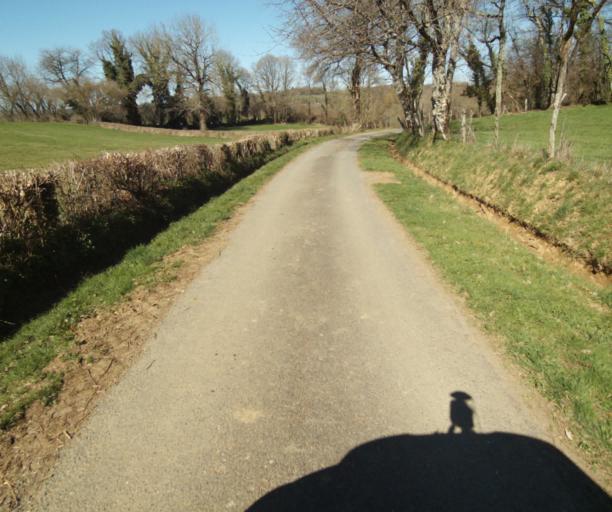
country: FR
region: Limousin
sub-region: Departement de la Correze
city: Saint-Clement
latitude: 45.3866
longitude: 1.6613
